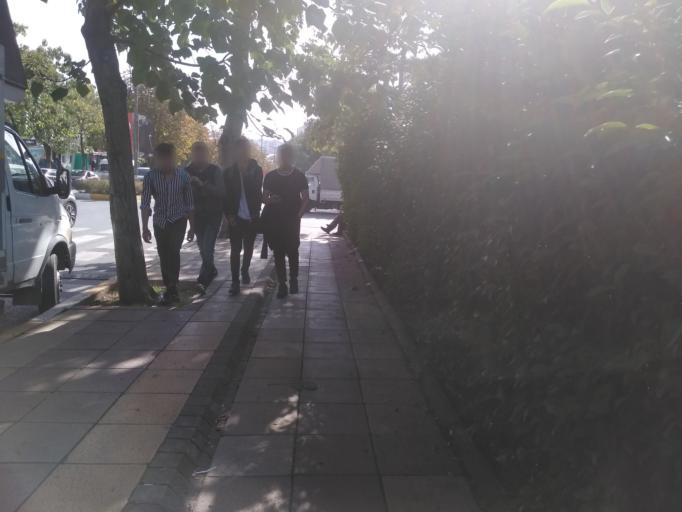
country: TR
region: Istanbul
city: Beylikduezue
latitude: 41.0077
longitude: 28.6433
